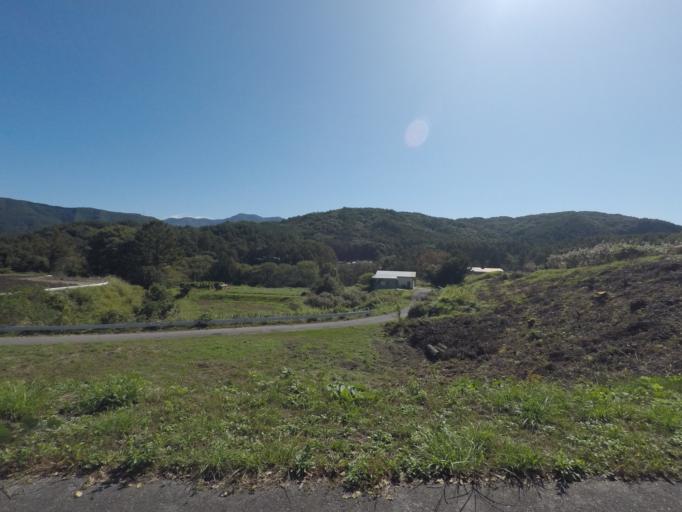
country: JP
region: Nagano
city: Ina
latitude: 35.9670
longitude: 137.7484
